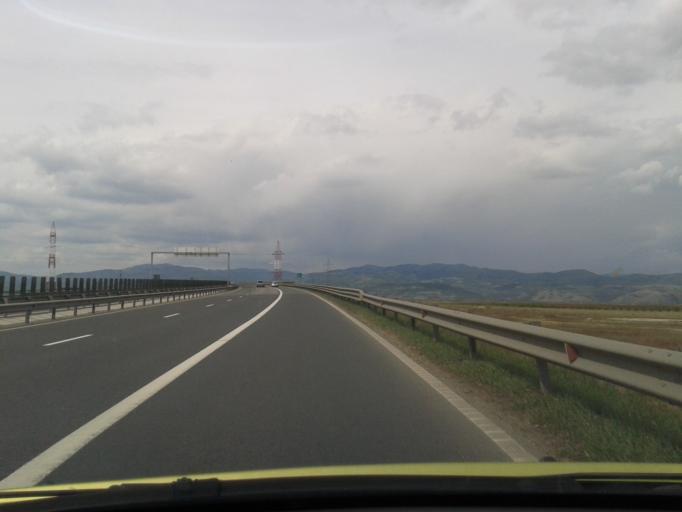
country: RO
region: Alba
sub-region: Municipiul Sebes
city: Lancram
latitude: 45.9774
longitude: 23.5537
